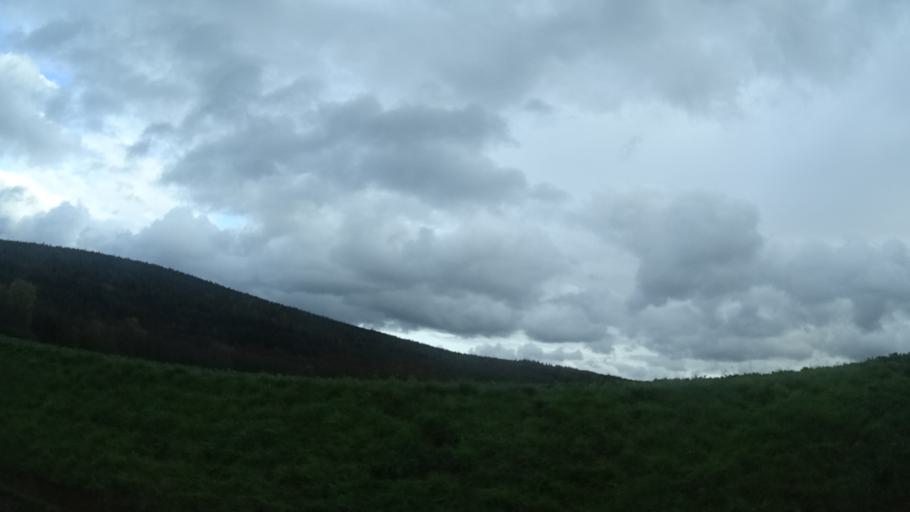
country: DE
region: Bavaria
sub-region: Regierungsbezirk Unterfranken
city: Hohenroth
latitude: 50.3536
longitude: 10.1351
